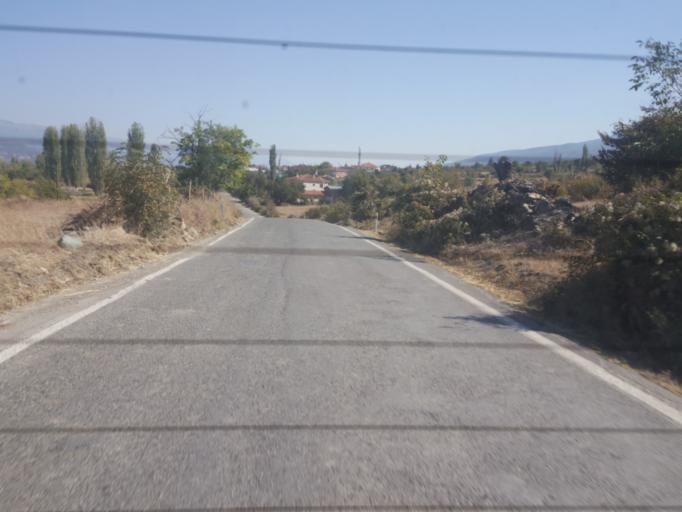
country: TR
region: Kastamonu
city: Tosya
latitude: 40.9878
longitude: 34.1086
